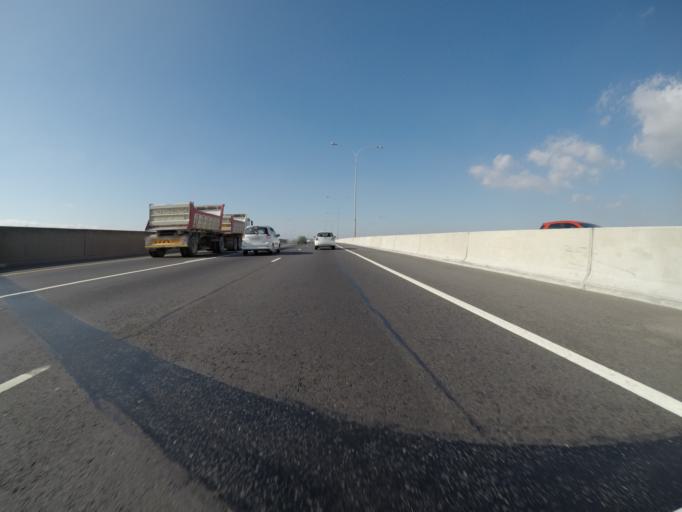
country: ZA
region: Western Cape
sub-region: City of Cape Town
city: Kraaifontein
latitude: -33.9193
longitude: 18.6655
